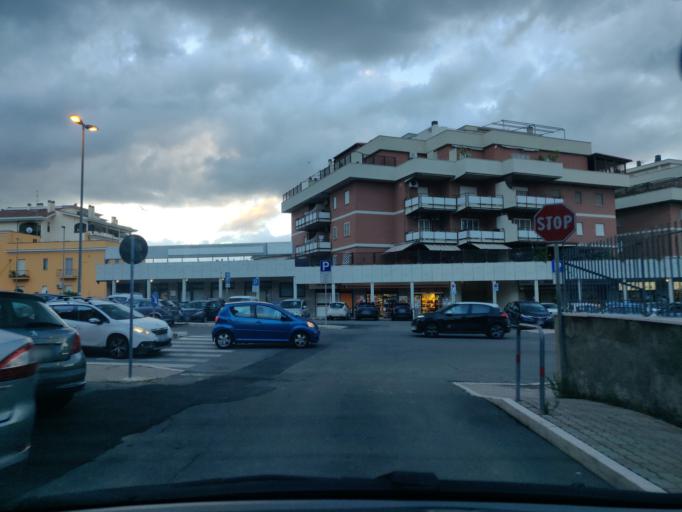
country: IT
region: Latium
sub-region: Citta metropolitana di Roma Capitale
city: Civitavecchia
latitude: 42.0922
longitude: 11.8057
